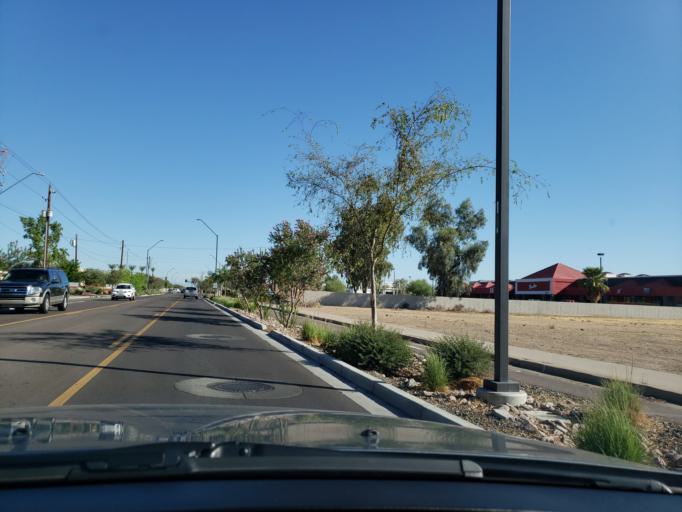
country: US
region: Arizona
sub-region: Maricopa County
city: Avondale
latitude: 33.4475
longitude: -112.3496
